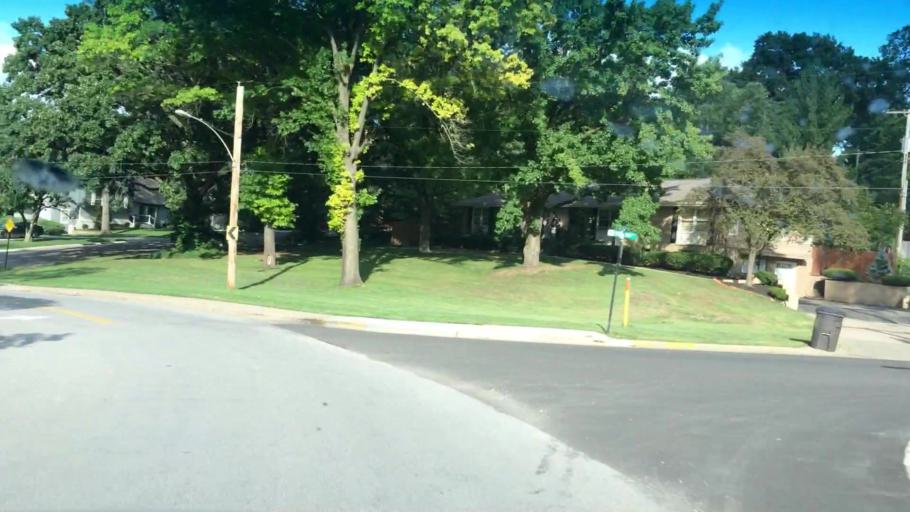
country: US
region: Kansas
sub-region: Johnson County
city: Fairway
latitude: 39.0261
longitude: -94.6279
